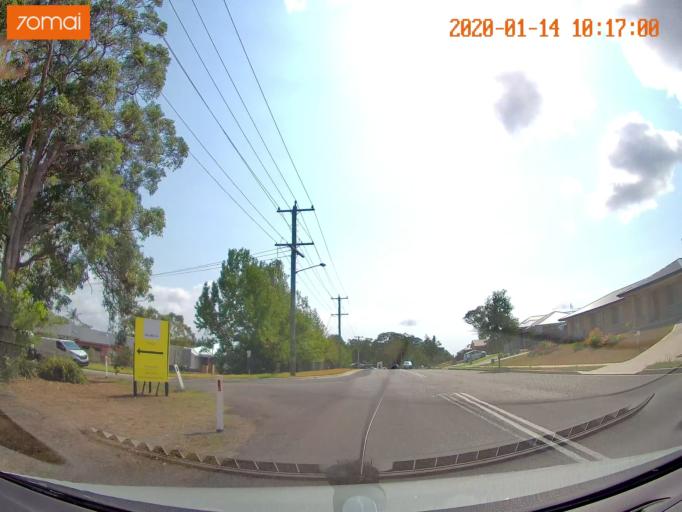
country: AU
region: New South Wales
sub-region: Lake Macquarie Shire
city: Dora Creek
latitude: -33.1092
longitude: 151.5054
